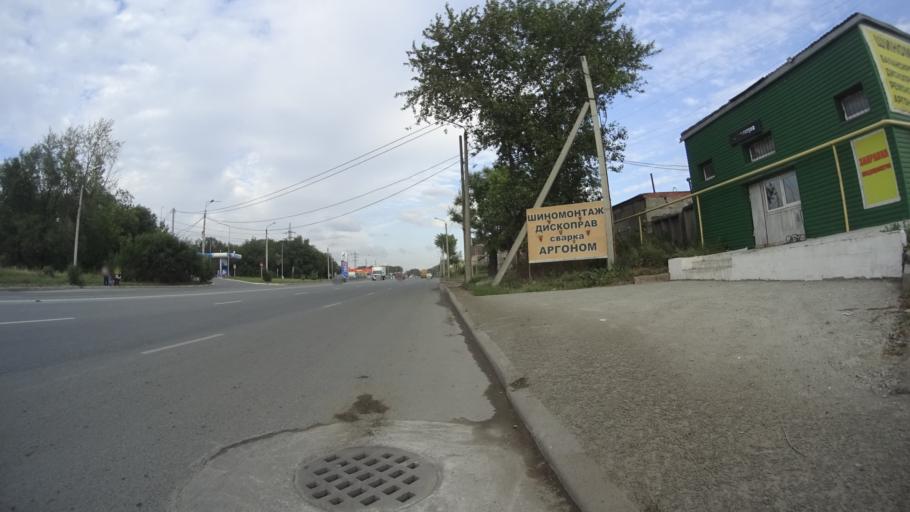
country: RU
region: Chelyabinsk
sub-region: Gorod Chelyabinsk
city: Chelyabinsk
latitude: 55.1919
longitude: 61.4245
